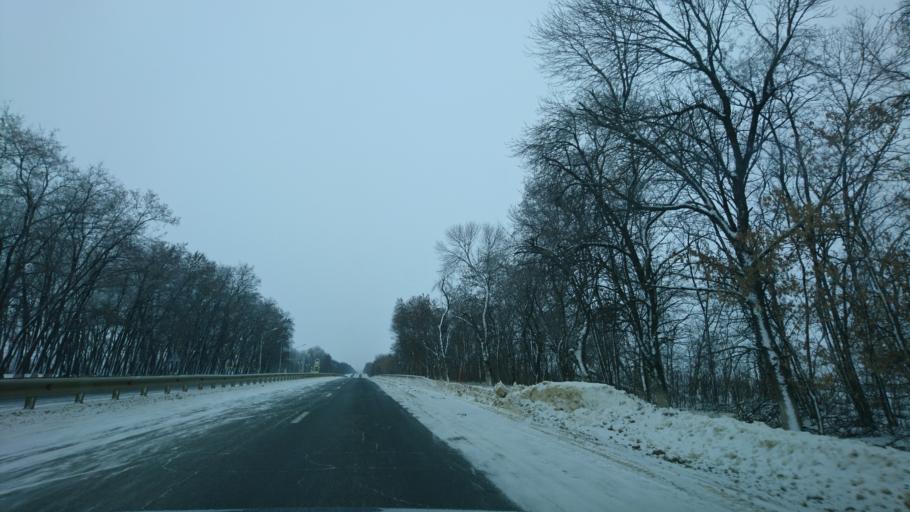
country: RU
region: Belgorod
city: Bessonovka
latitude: 50.3698
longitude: 36.3217
